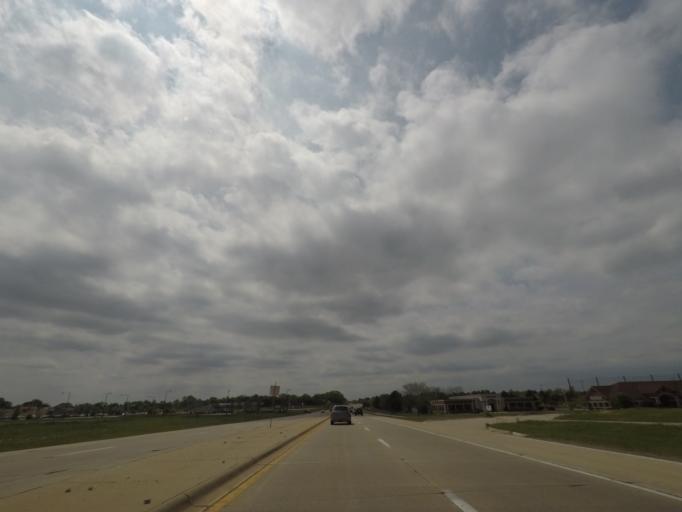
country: US
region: Illinois
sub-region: Winnebago County
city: Cherry Valley
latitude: 42.2956
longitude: -88.9801
